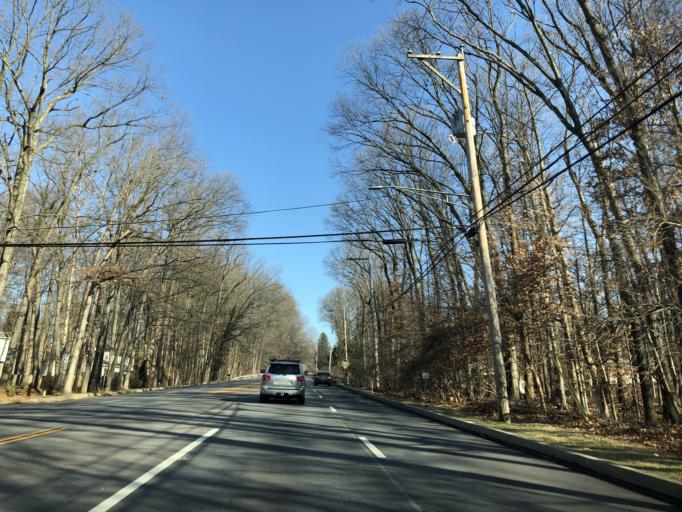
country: US
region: Pennsylvania
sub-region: Chester County
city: Downingtown
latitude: 40.0380
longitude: -75.6719
